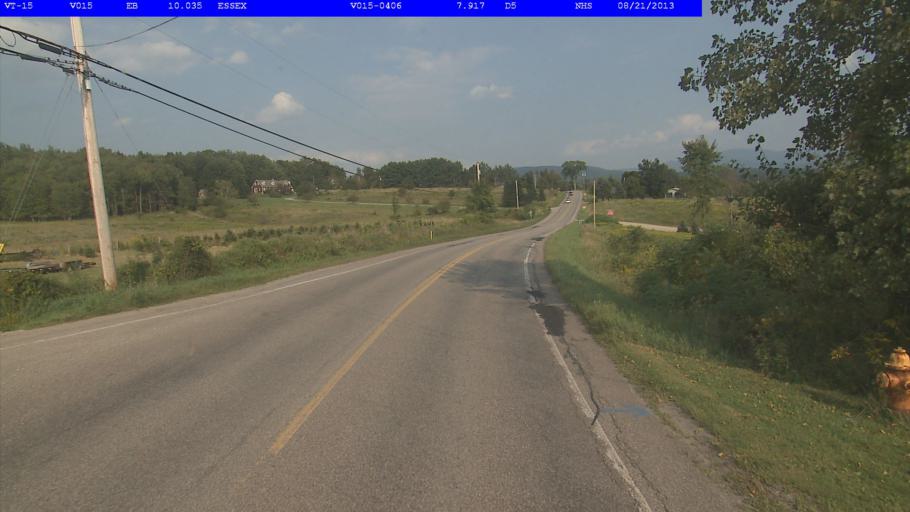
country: US
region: Vermont
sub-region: Chittenden County
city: Jericho
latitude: 44.5032
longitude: -73.0109
